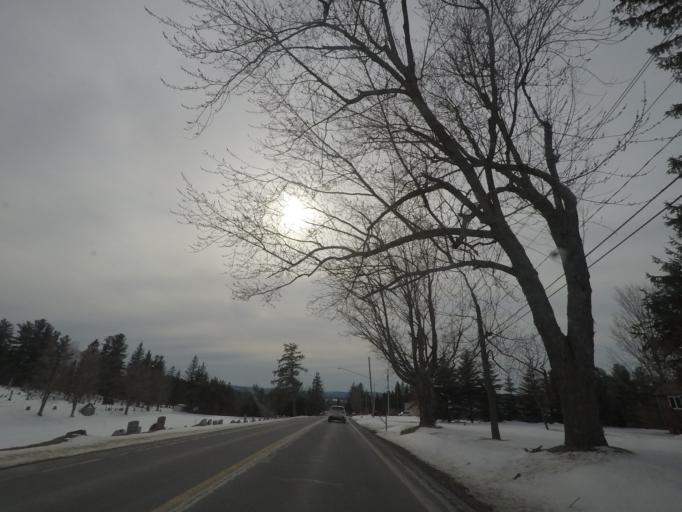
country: US
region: New York
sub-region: Albany County
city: Altamont
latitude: 42.6753
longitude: -74.1096
